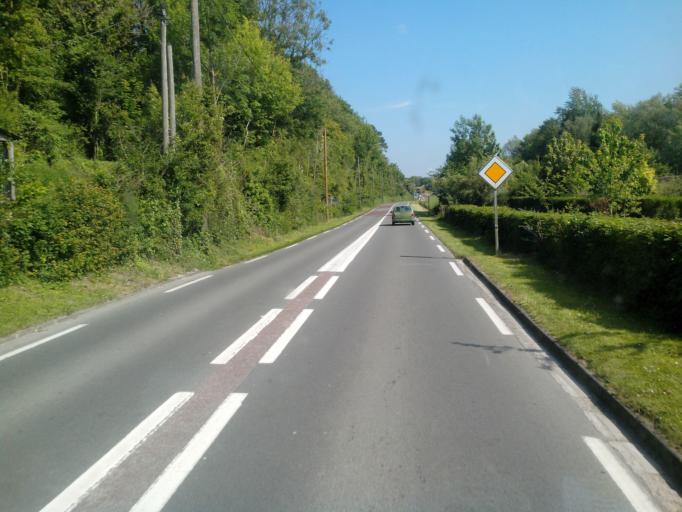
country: FR
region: Picardie
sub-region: Departement de la Somme
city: Sailly-Flibeaucourt
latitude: 50.1489
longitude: 1.7525
